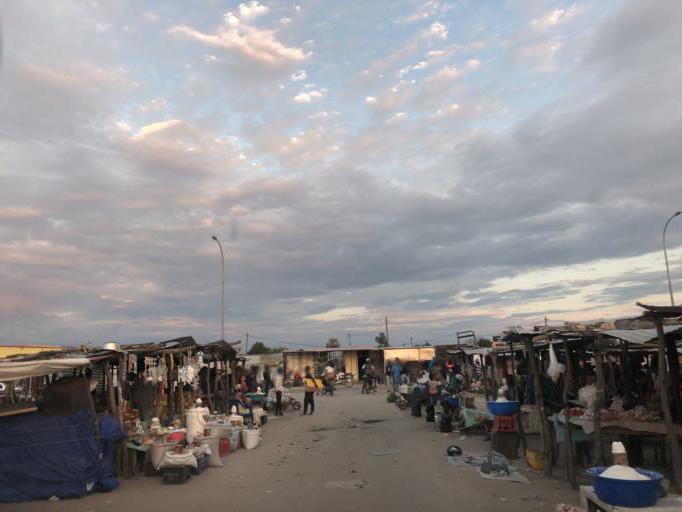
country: AO
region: Cunene
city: Ondjiva
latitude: -17.0776
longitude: 15.7045
